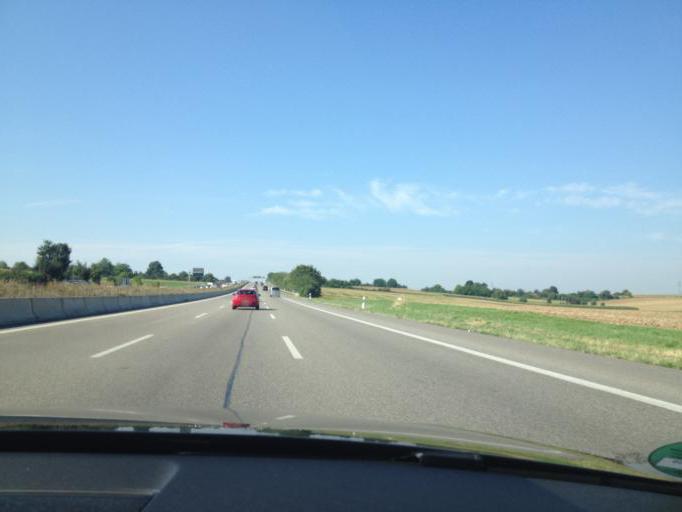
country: DE
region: Baden-Wuerttemberg
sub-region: Regierungsbezirk Stuttgart
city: Korntal
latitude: 48.8412
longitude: 9.1072
